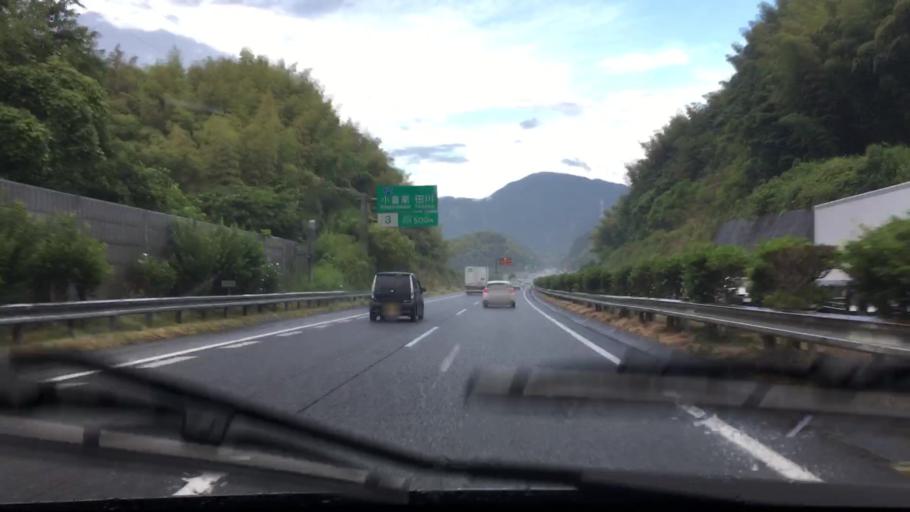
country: JP
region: Fukuoka
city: Kitakyushu
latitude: 33.8070
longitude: 130.8450
